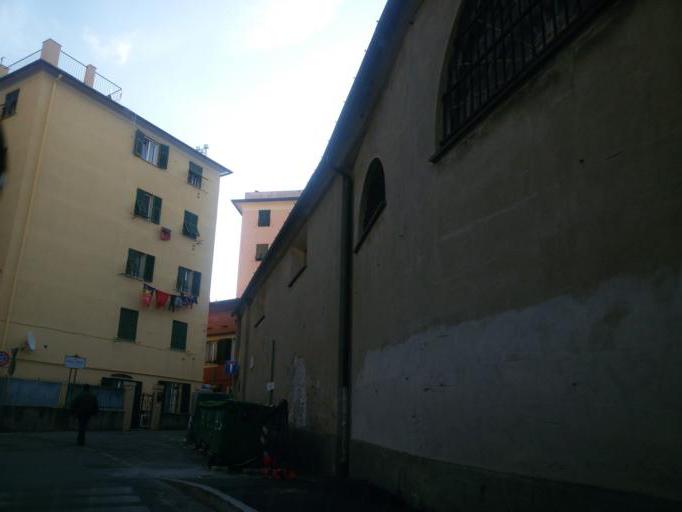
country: IT
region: Liguria
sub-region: Provincia di Genova
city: Genoa
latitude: 44.3952
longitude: 8.9884
